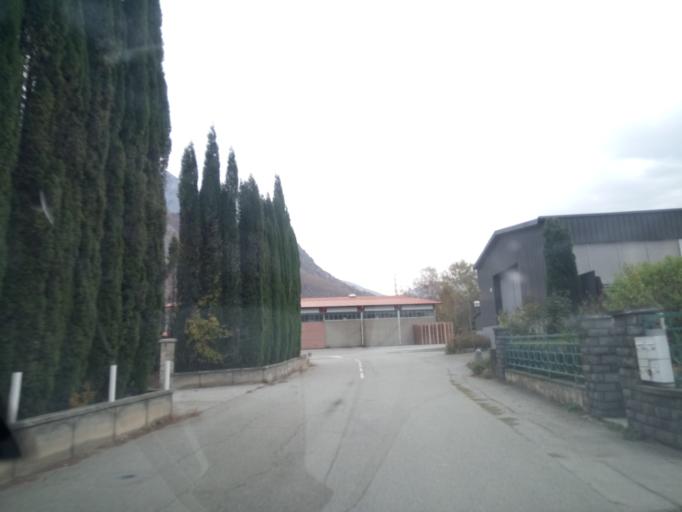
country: FR
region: Rhone-Alpes
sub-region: Departement de la Savoie
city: Villargondran
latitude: 45.2654
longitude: 6.3785
